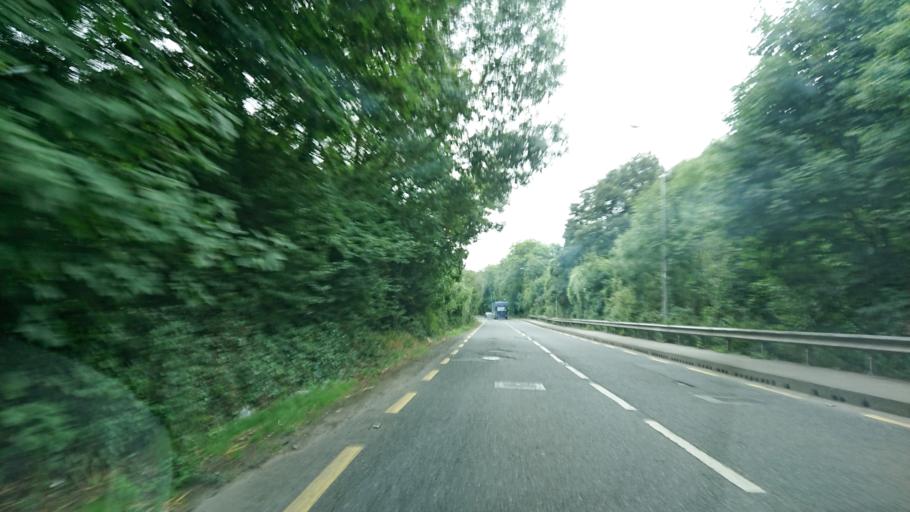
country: IE
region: Munster
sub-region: County Cork
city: Mallow
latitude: 52.1413
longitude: -8.6370
